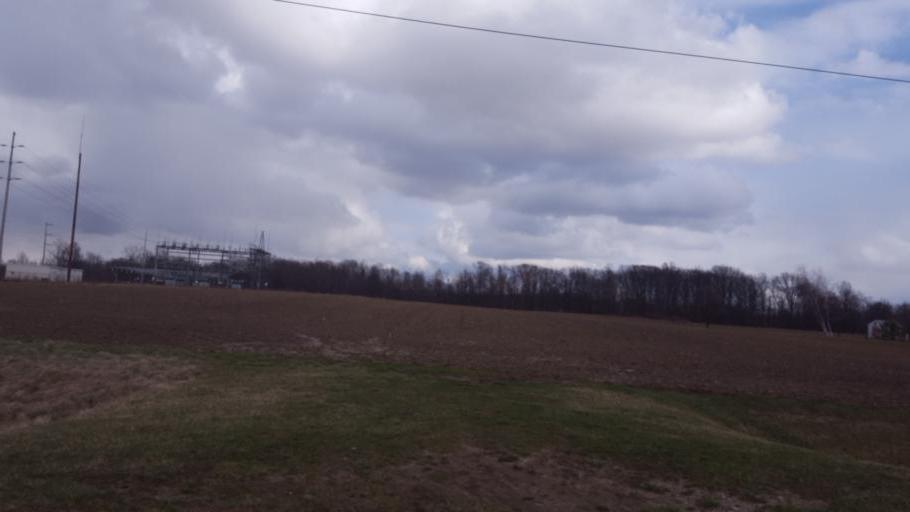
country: US
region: Ohio
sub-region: Crawford County
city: Crestline
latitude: 40.7646
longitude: -82.6982
